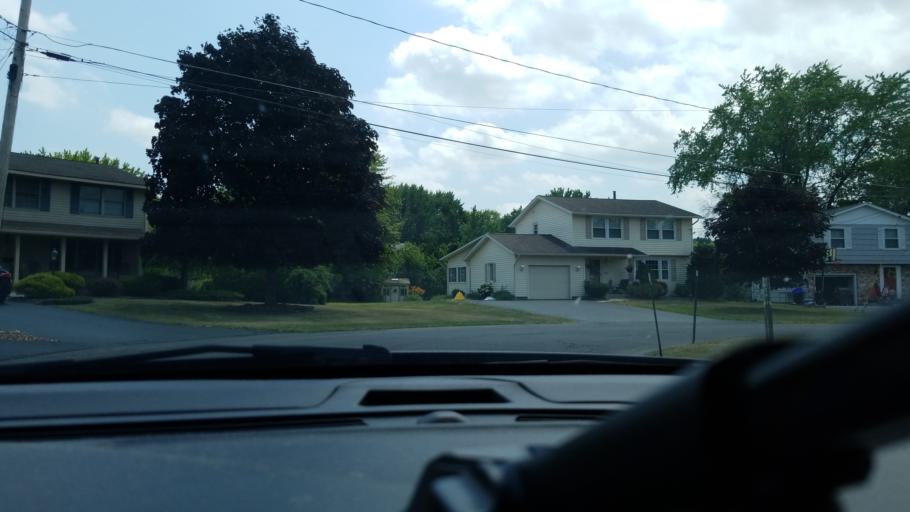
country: US
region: New York
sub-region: Onondaga County
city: Galeville
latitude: 43.1075
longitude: -76.1738
